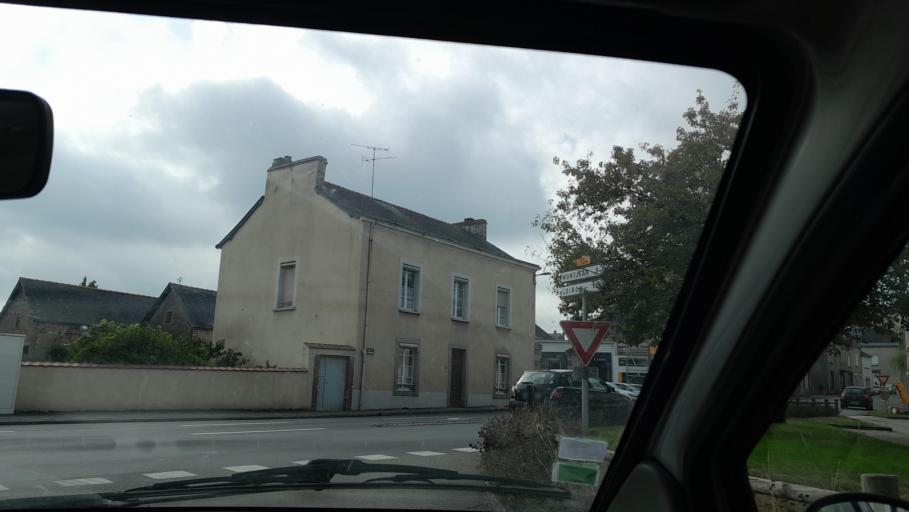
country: FR
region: Pays de la Loire
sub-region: Departement de la Mayenne
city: Cosse-le-Vivien
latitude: 47.9484
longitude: -0.9097
